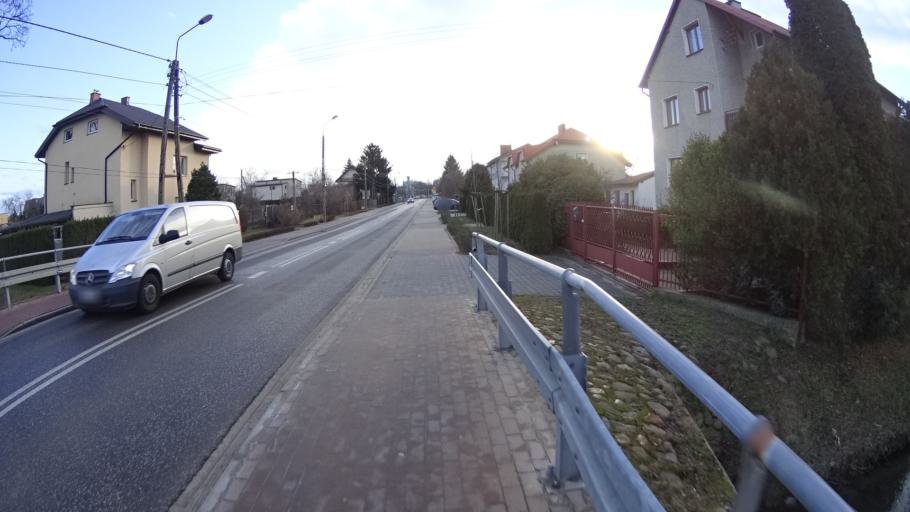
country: PL
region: Masovian Voivodeship
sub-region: Powiat warszawski zachodni
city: Ozarow Mazowiecki
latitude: 52.2163
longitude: 20.7997
